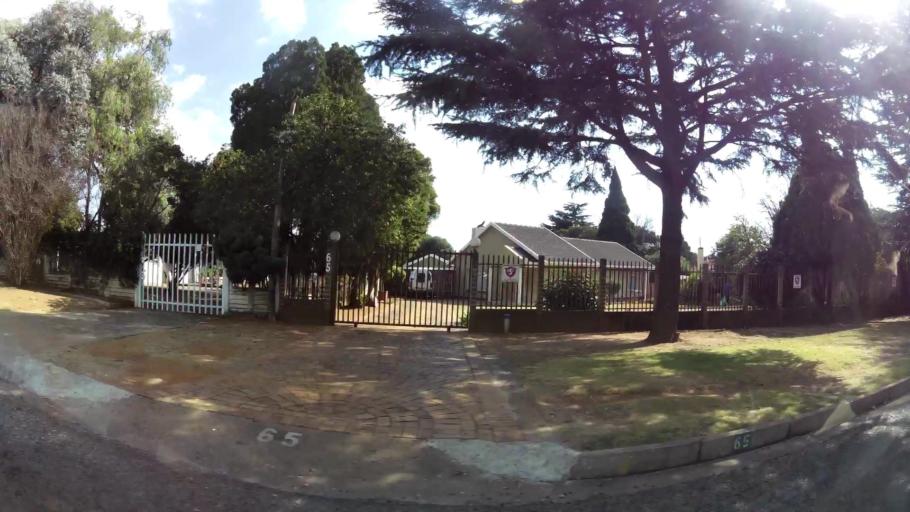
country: ZA
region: Gauteng
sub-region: City of Johannesburg Metropolitan Municipality
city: Modderfontein
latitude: -26.0873
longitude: 28.2335
